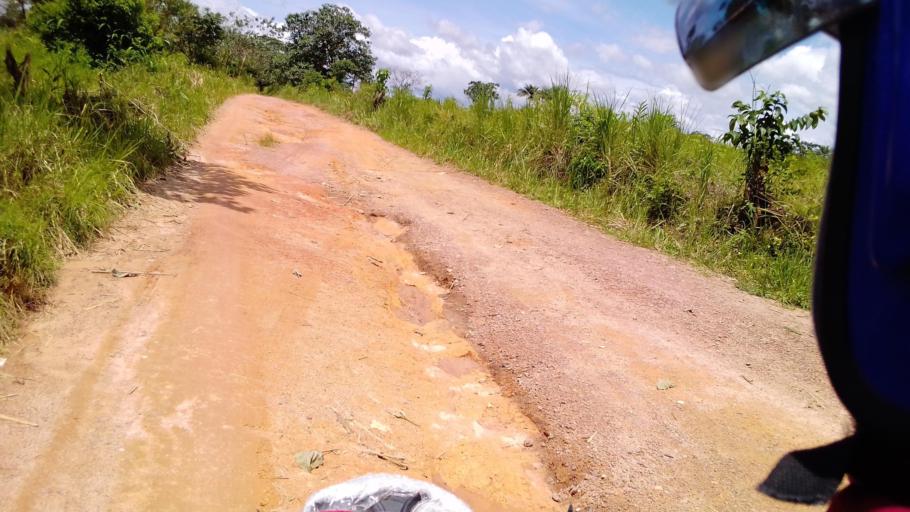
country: SL
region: Eastern Province
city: Koidu
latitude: 8.6922
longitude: -10.9542
